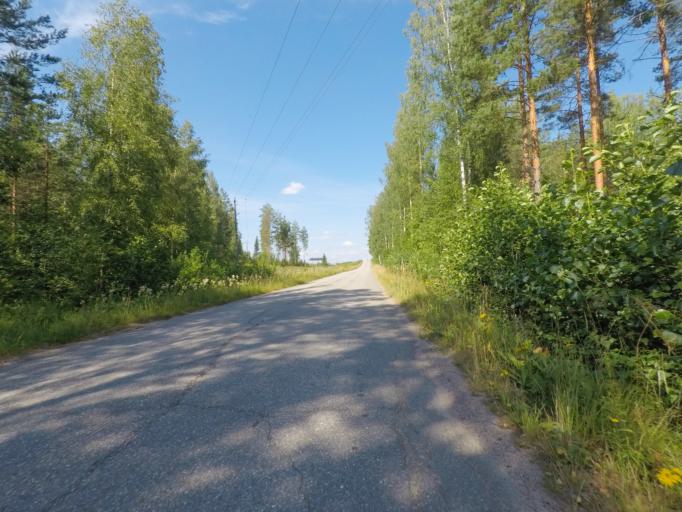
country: FI
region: Southern Savonia
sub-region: Mikkeli
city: Puumala
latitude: 61.4116
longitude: 28.0925
